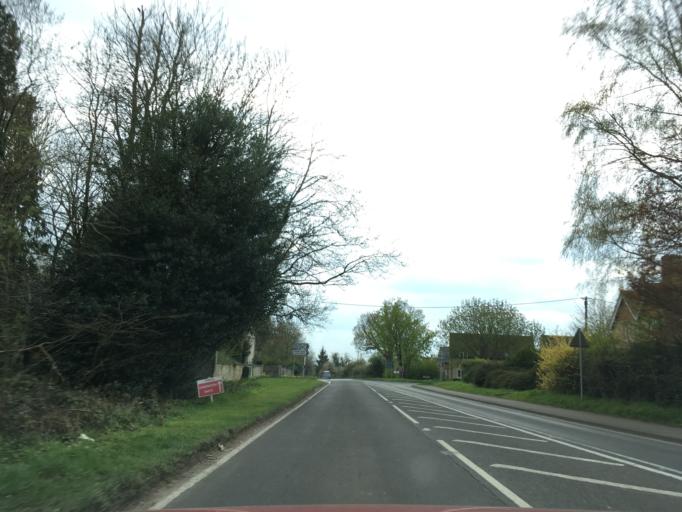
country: GB
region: England
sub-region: Oxfordshire
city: North Leigh
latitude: 51.8139
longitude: -1.4291
